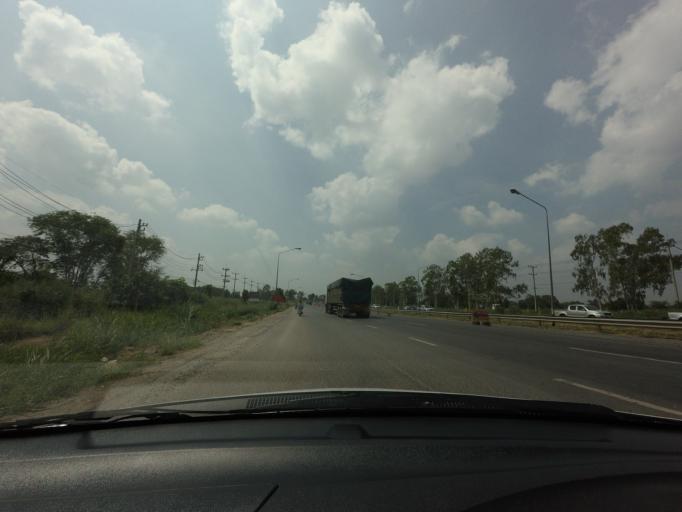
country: TH
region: Nakhon Ratchasima
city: Pak Chong
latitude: 14.6734
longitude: 101.4553
